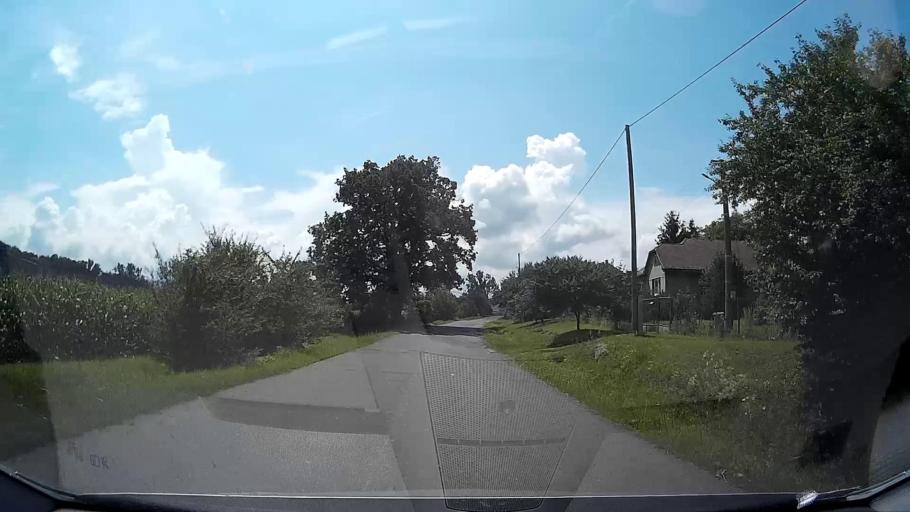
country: SK
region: Banskobystricky
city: Fil'akovo
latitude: 48.3198
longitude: 19.8128
